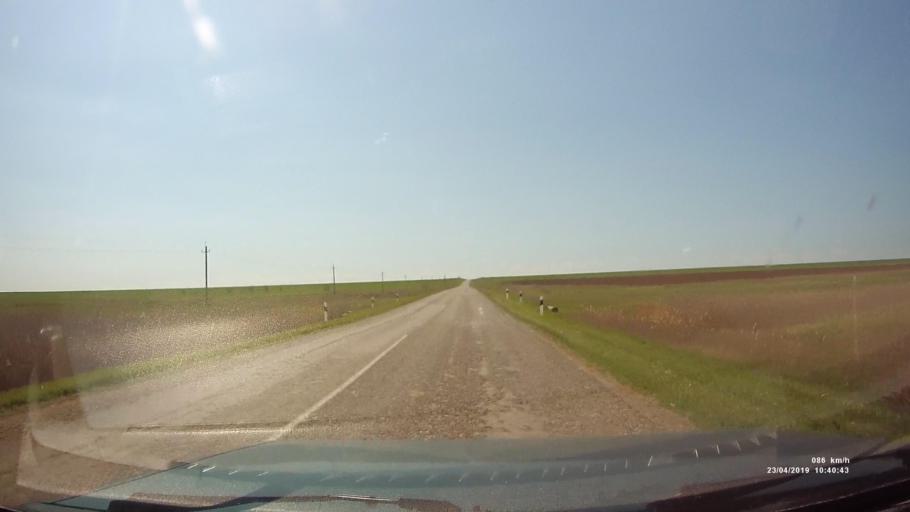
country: RU
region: Kalmykiya
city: Yashalta
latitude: 46.5028
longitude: 42.6384
